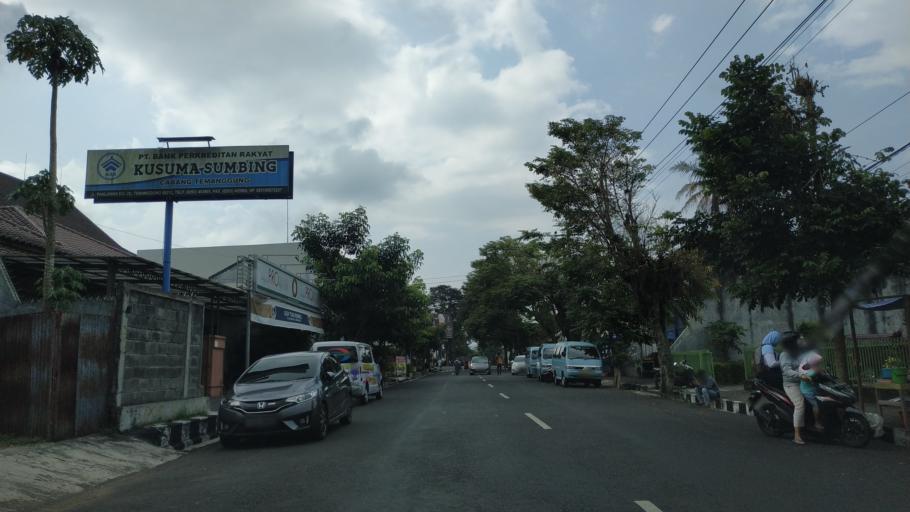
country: ID
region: Central Java
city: Magelang
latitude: -7.3176
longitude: 110.1770
